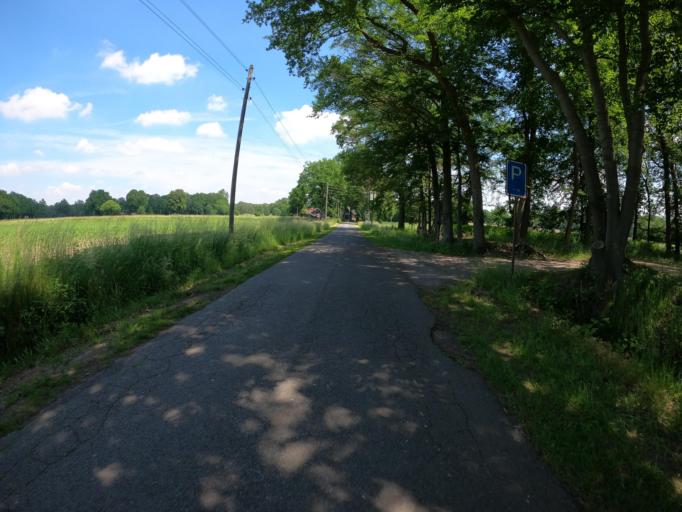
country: DE
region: North Rhine-Westphalia
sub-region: Regierungsbezirk Dusseldorf
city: Hunxe
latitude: 51.6958
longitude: 6.8025
